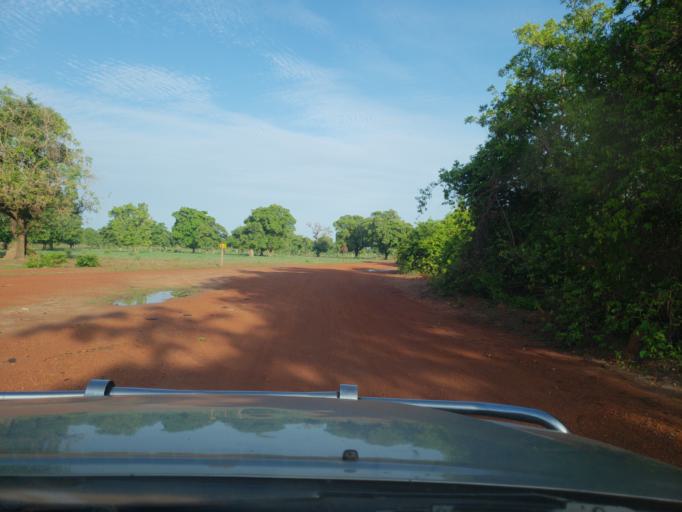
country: ML
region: Sikasso
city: Koutiala
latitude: 12.4227
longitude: -5.5875
